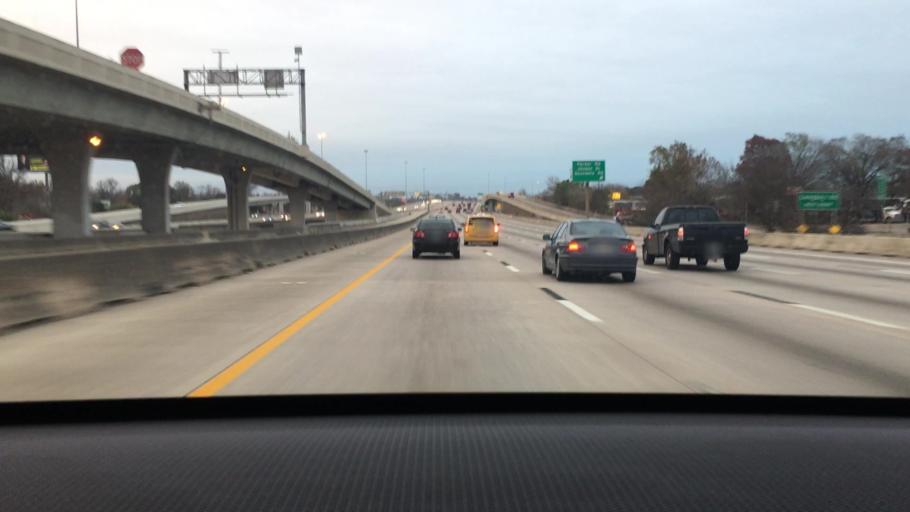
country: US
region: Texas
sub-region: Harris County
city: Houston
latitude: 29.8509
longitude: -95.3335
